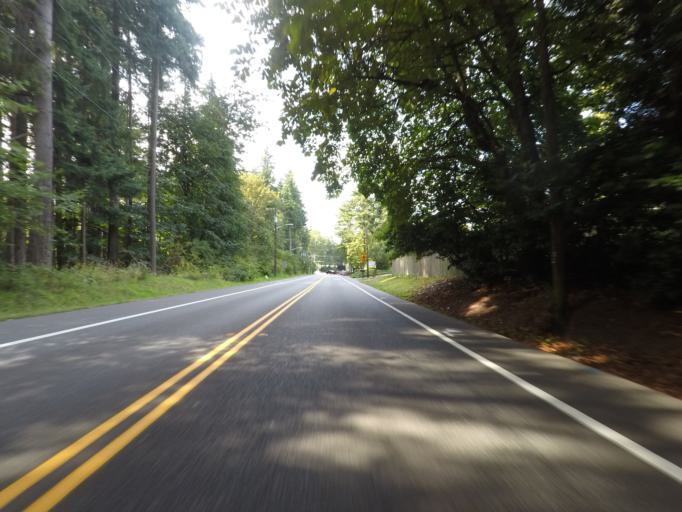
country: US
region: Washington
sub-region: King County
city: Kenmore
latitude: 47.7360
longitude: -122.2486
